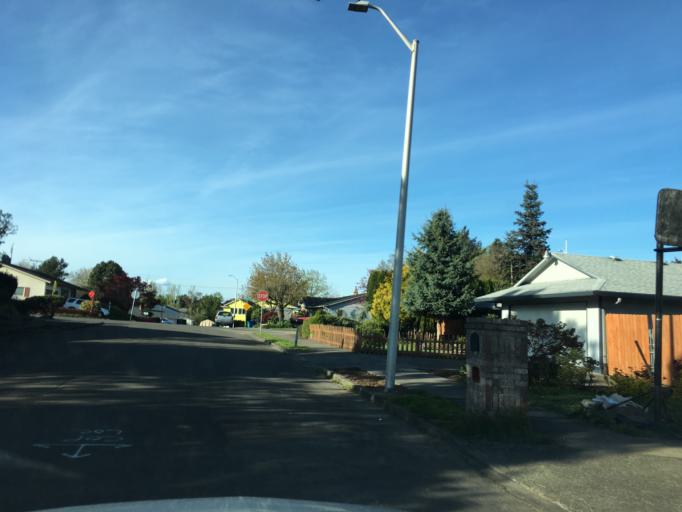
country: US
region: Oregon
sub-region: Multnomah County
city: Lents
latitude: 45.5522
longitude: -122.5233
